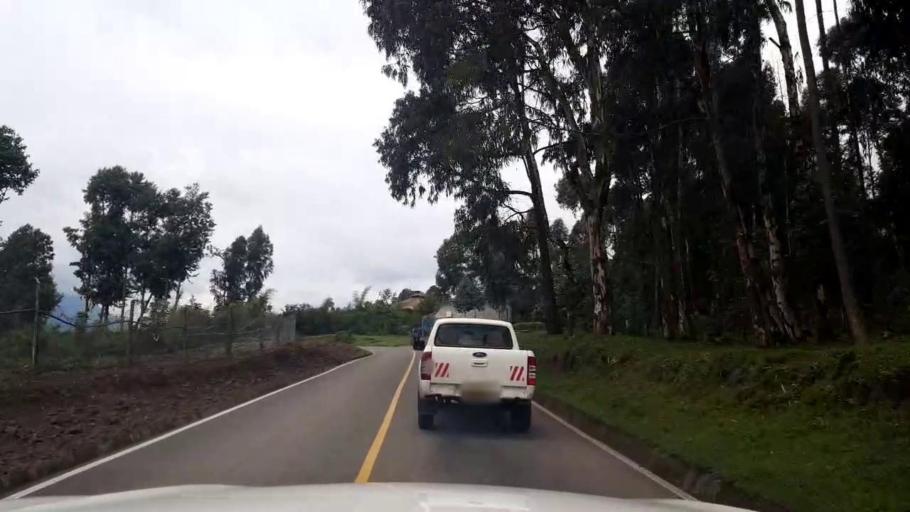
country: RW
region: Northern Province
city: Musanze
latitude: -1.4301
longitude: 29.5623
